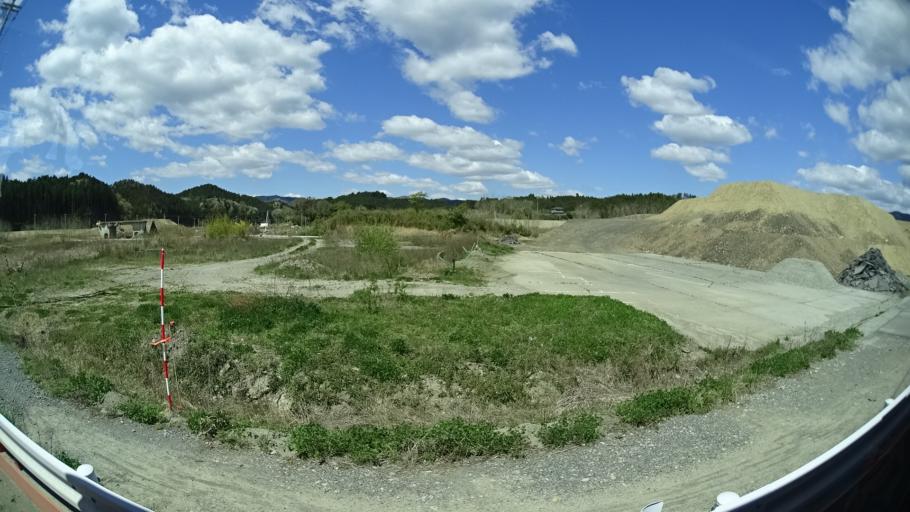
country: JP
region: Miyagi
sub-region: Oshika Gun
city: Onagawa Cho
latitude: 38.6758
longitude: 141.4436
